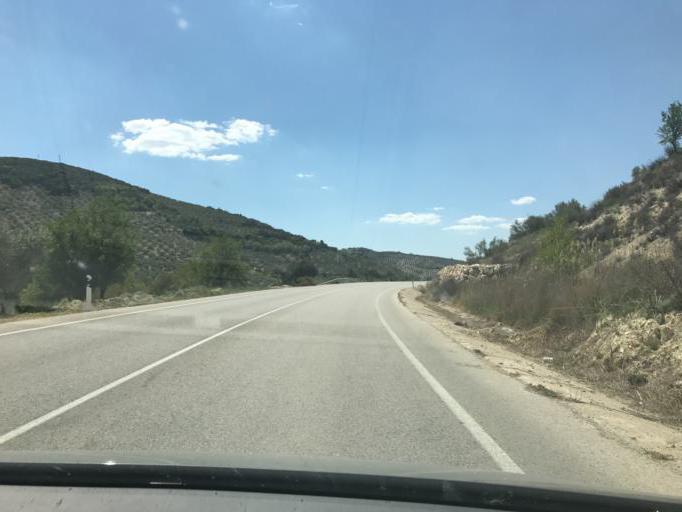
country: ES
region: Andalusia
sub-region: Provincia de Granada
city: Benalua de las Villas
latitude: 37.4399
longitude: -3.6535
